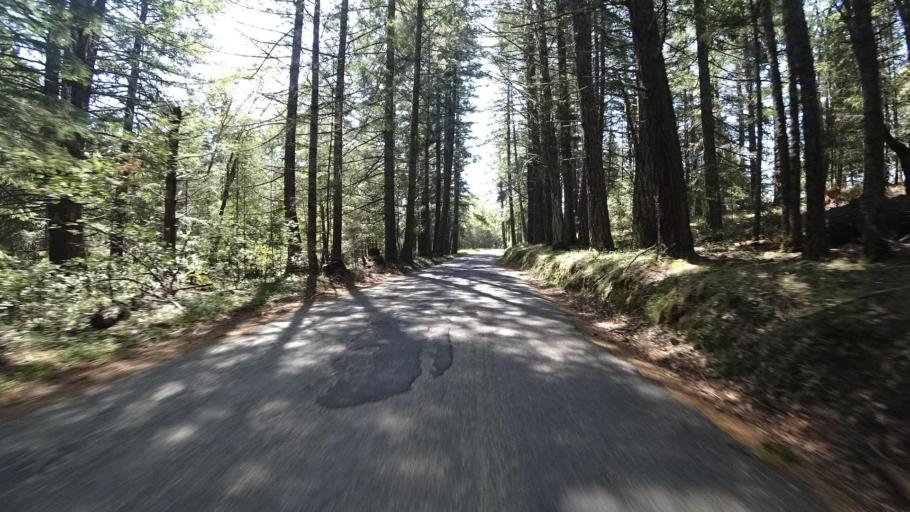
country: US
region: California
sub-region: Humboldt County
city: Redway
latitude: 40.0332
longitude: -123.6386
